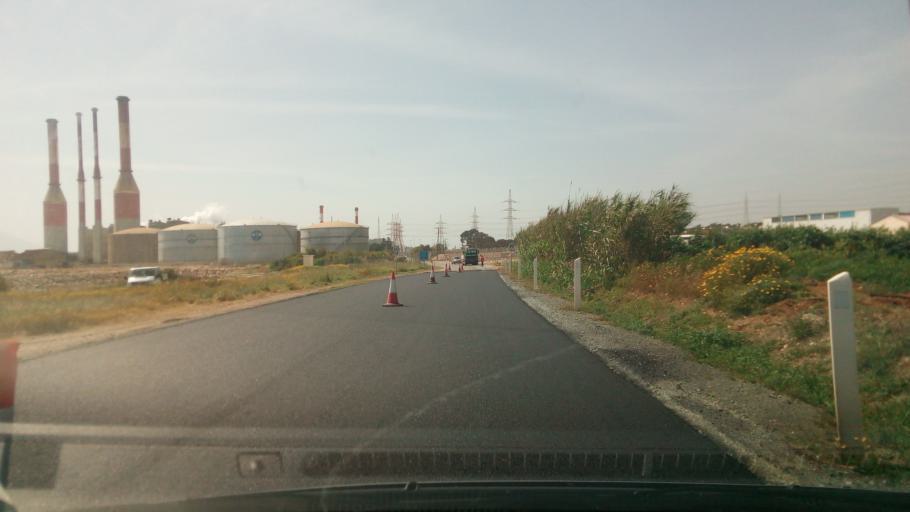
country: CY
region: Larnaka
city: Xylotymbou
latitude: 34.9824
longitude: 33.7520
